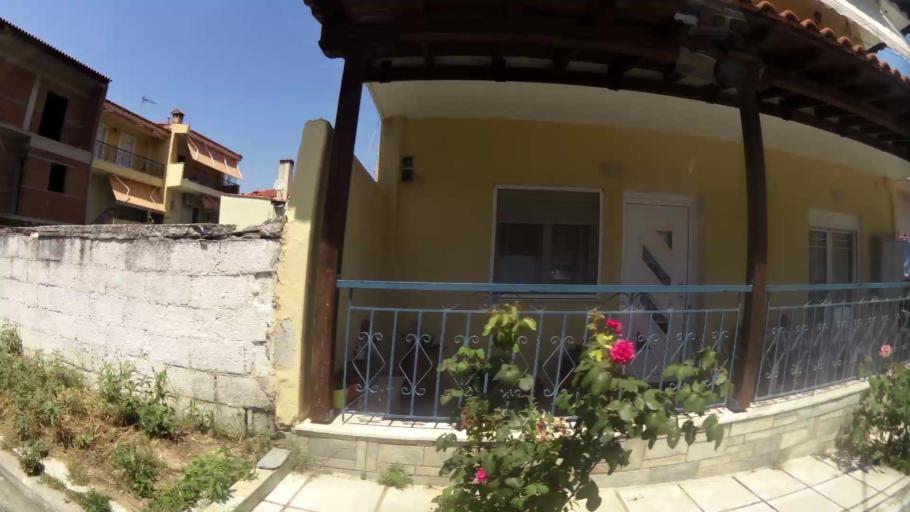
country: GR
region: Central Macedonia
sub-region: Nomos Thessalonikis
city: Trilofos
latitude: 40.4759
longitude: 22.9718
